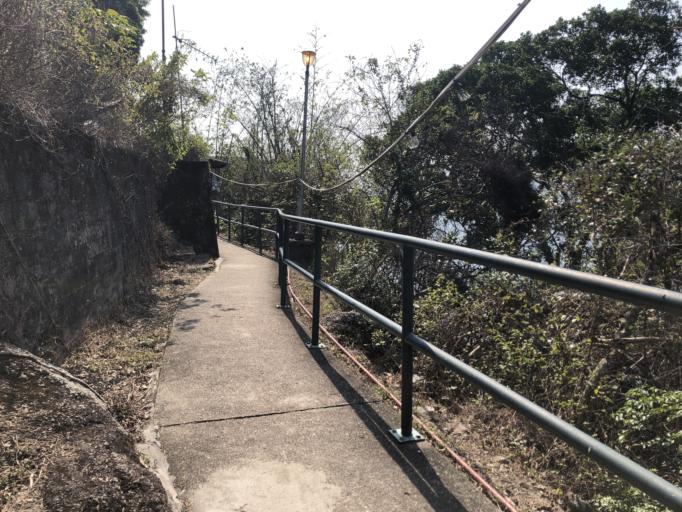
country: HK
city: Sok Kwu Wan
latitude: 22.1642
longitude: 114.2542
